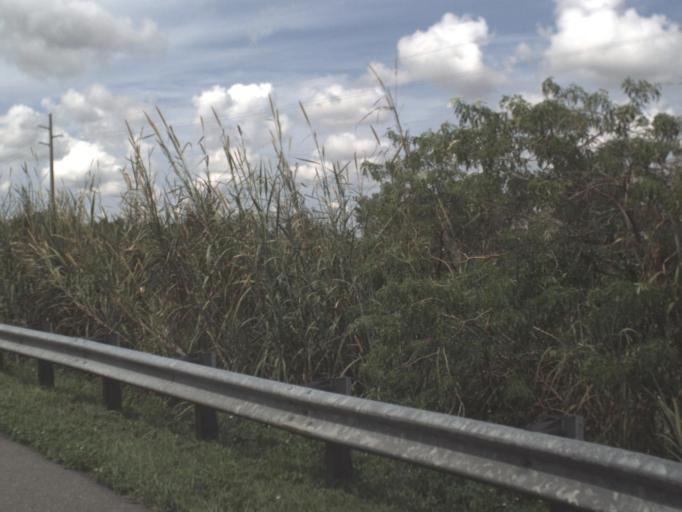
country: US
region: Florida
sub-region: Highlands County
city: Lake Placid
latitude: 27.2097
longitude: -81.1634
